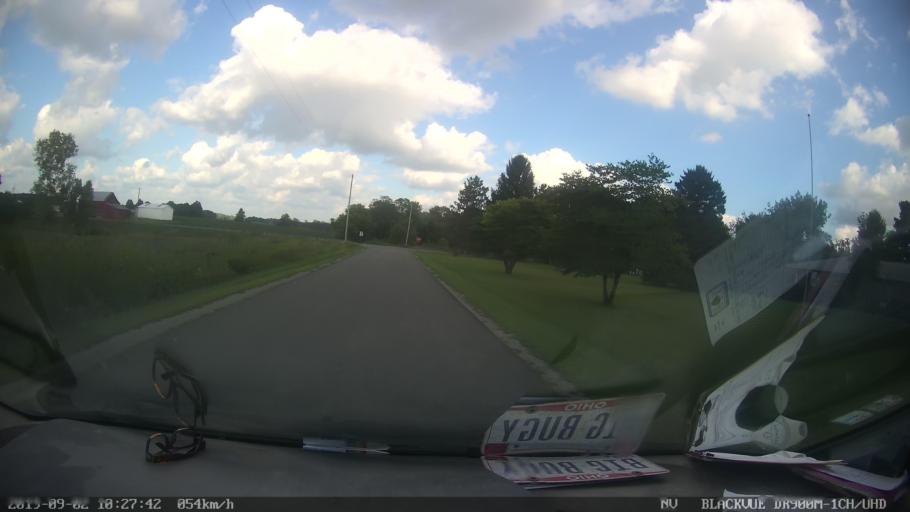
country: US
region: Ohio
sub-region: Morrow County
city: Cardington
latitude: 40.4872
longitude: -82.9659
